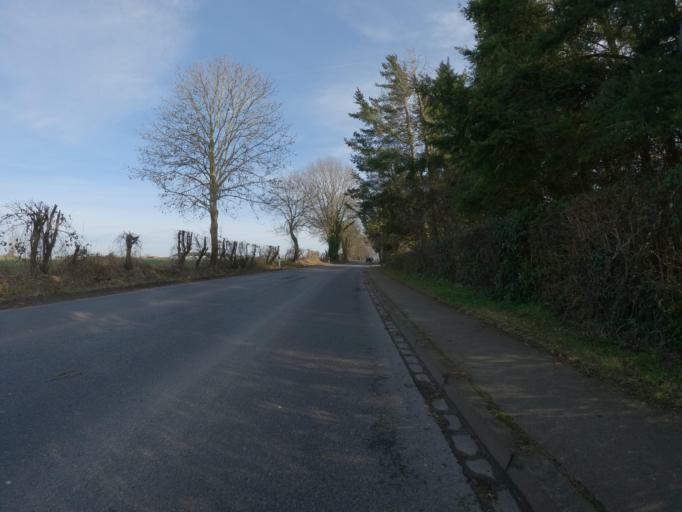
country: DE
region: North Rhine-Westphalia
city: Stolberg
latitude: 50.7335
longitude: 6.1668
